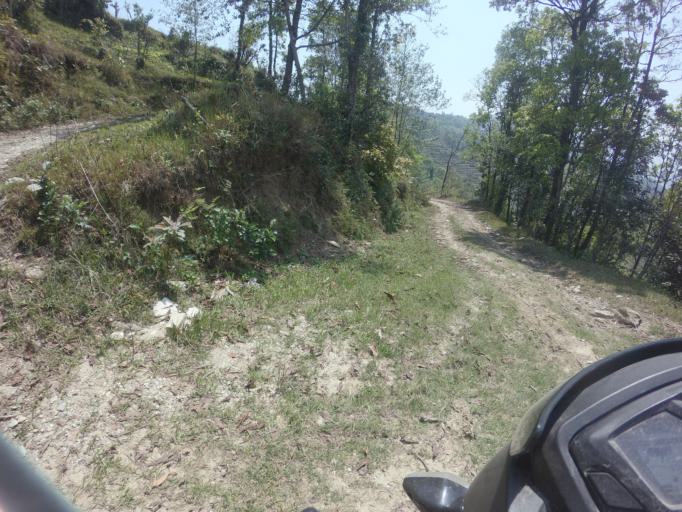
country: NP
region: Western Region
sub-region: Gandaki Zone
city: Pokhara
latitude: 28.3028
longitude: 83.9656
